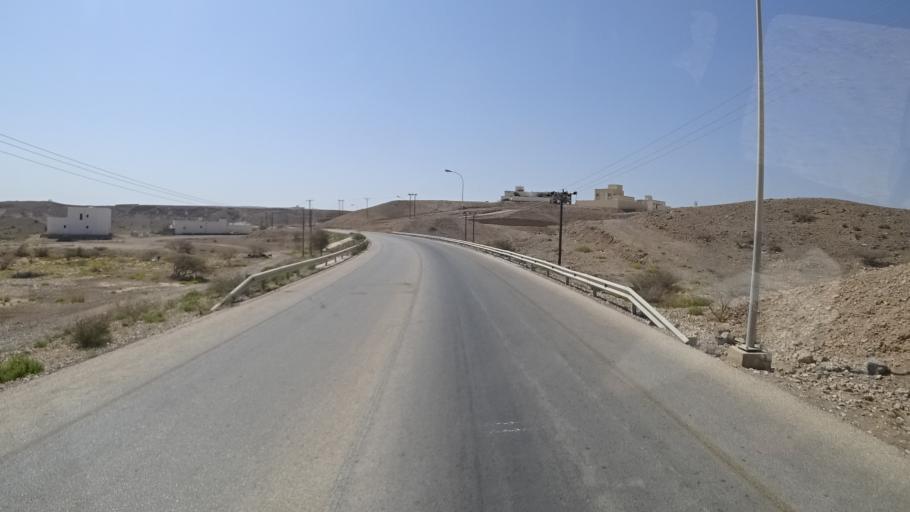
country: OM
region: Ash Sharqiyah
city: Sur
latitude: 22.5443
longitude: 59.5013
